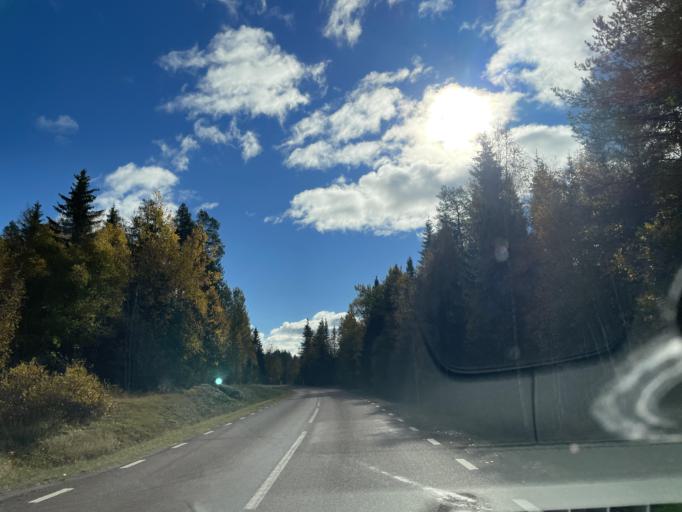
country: NO
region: Hedmark
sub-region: Trysil
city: Innbygda
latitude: 61.4950
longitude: 13.0771
